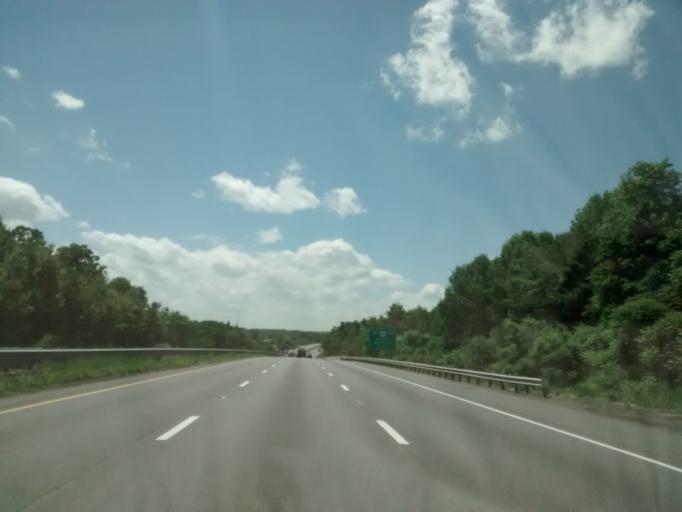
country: US
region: Massachusetts
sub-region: Worcester County
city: Auburn
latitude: 42.2047
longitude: -71.8114
